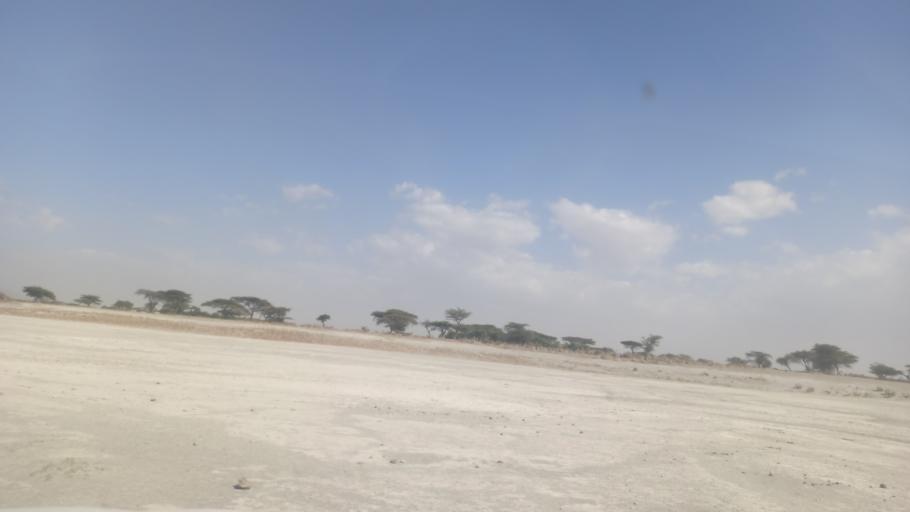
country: ET
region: Oromiya
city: Ziway
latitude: 7.6875
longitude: 38.6543
